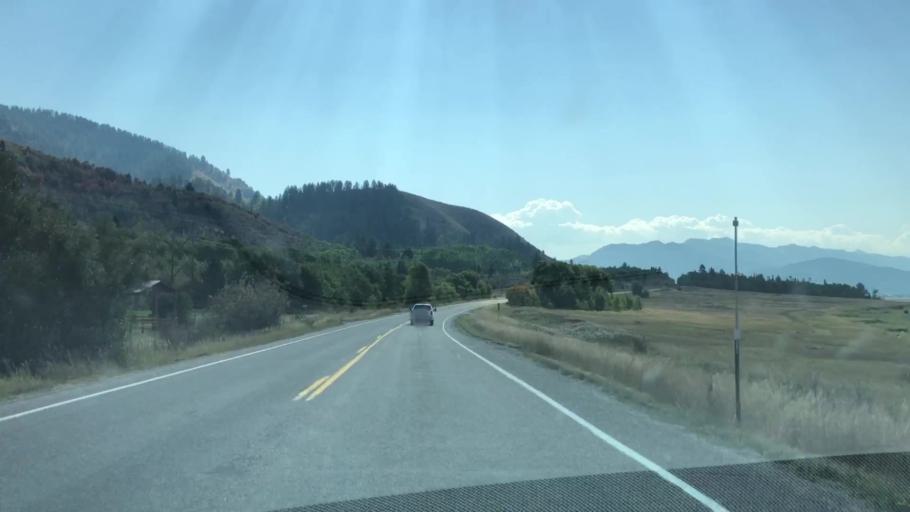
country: US
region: Wyoming
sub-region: Teton County
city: Hoback
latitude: 43.2167
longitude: -111.0655
